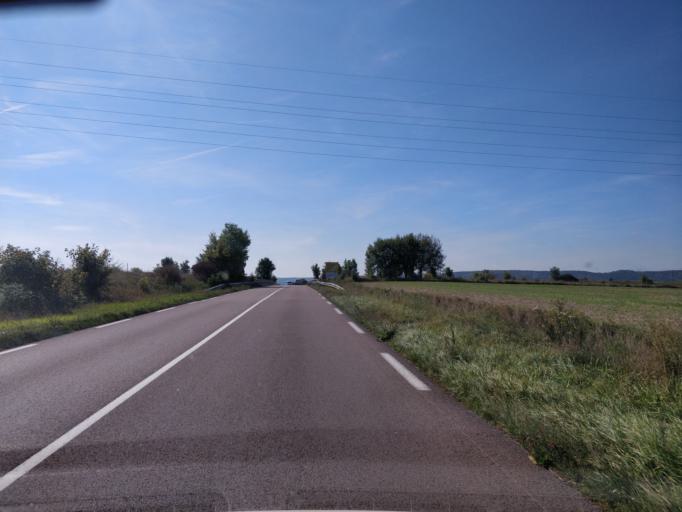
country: FR
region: Champagne-Ardenne
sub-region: Departement de l'Aube
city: Saint-Pouange
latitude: 48.2371
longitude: 4.0201
